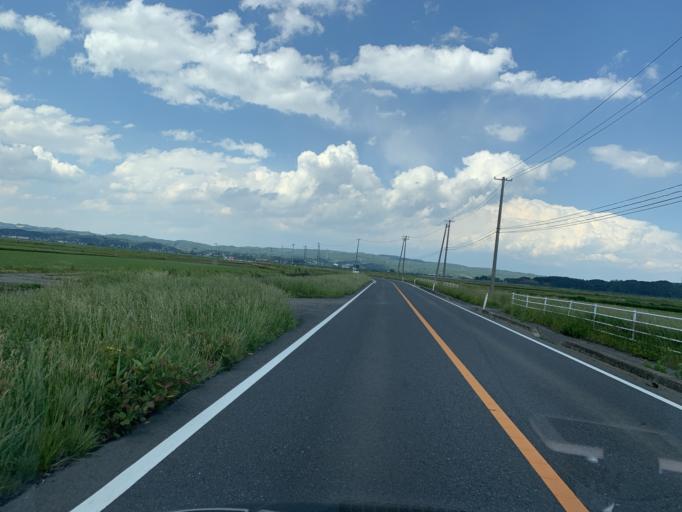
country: JP
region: Miyagi
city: Wakuya
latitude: 38.5134
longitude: 141.1249
